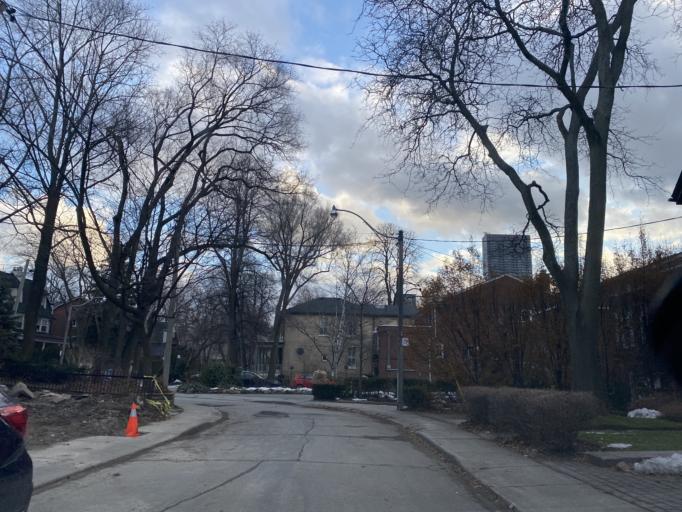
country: CA
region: Ontario
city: Toronto
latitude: 43.6768
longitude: -79.3770
